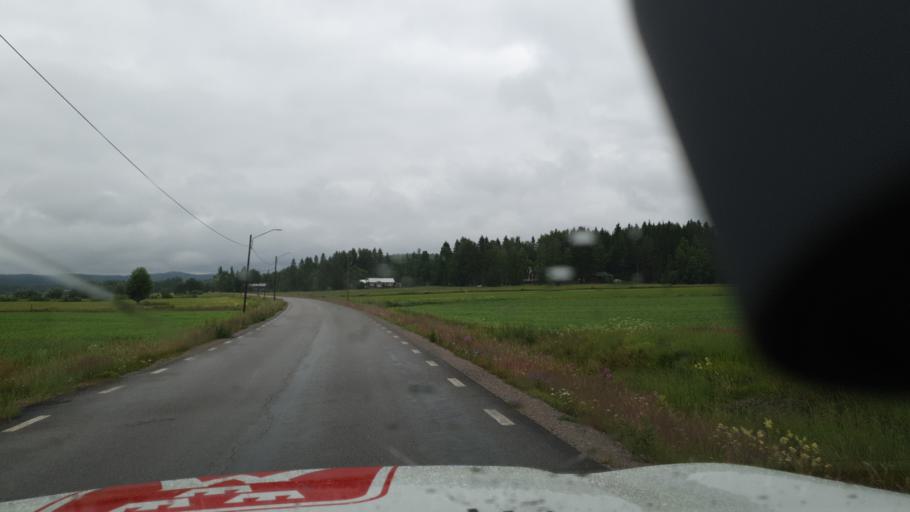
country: SE
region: Vaesterbotten
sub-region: Vannas Kommun
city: Vannasby
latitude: 63.7827
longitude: 19.8653
